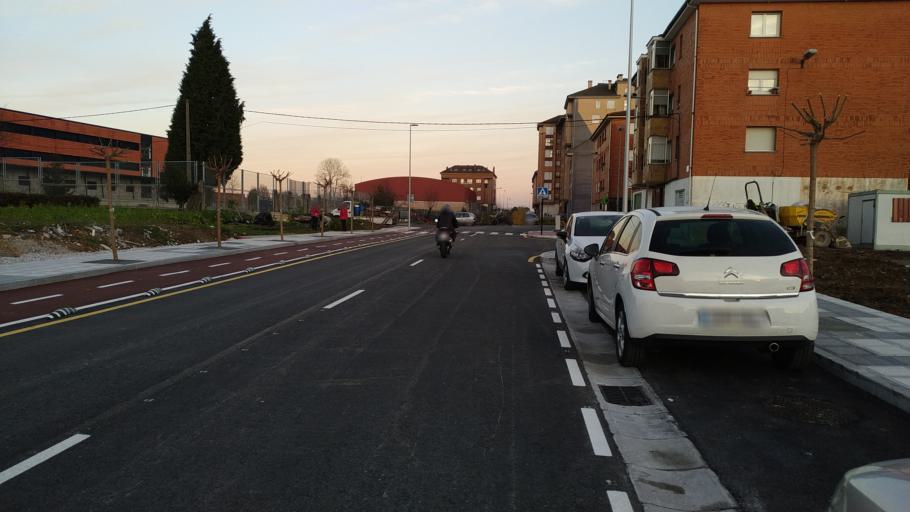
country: ES
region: Asturias
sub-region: Province of Asturias
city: Lugones
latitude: 43.4009
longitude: -5.8056
